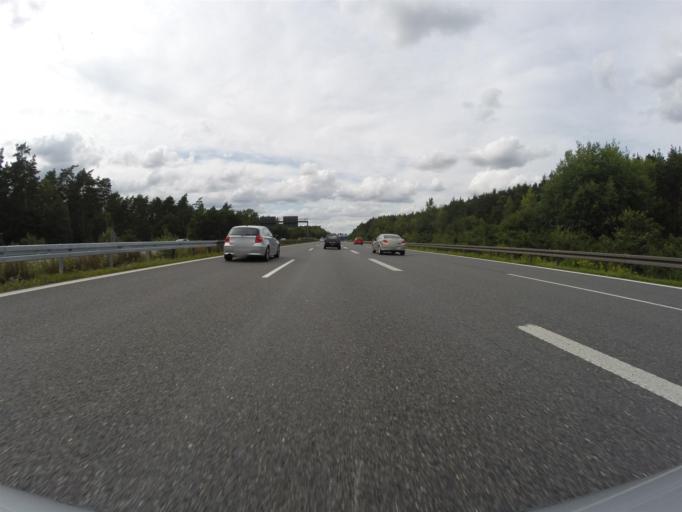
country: DE
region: Bavaria
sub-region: Regierungsbezirk Mittelfranken
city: Wendelstein
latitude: 49.3849
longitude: 11.1257
